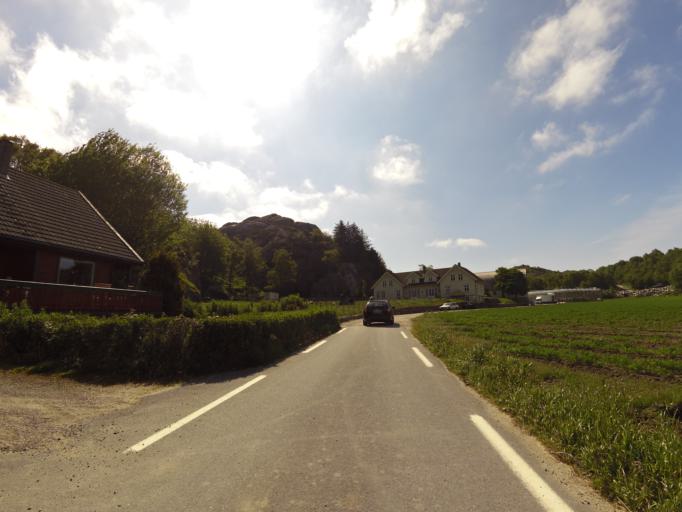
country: NO
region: Rogaland
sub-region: Ha
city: Vigrestad
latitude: 58.5164
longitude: 5.8225
